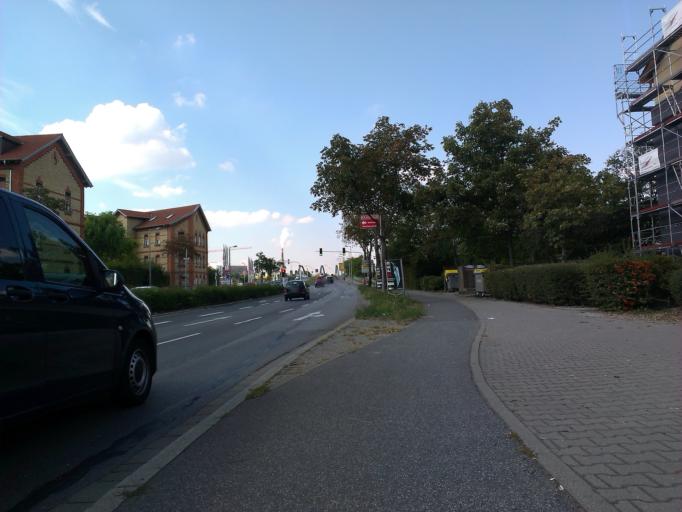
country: DE
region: Baden-Wuerttemberg
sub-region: Karlsruhe Region
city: Mannheim
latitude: 49.5298
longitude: 8.4868
